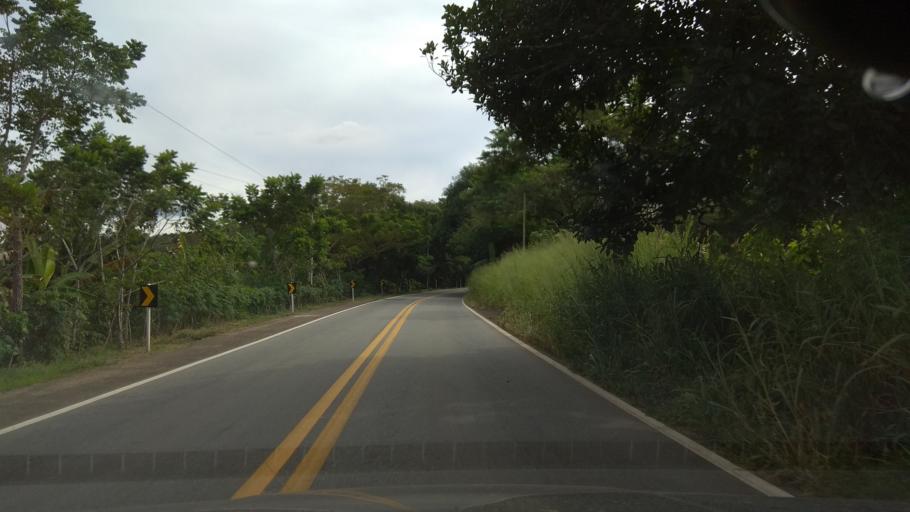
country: BR
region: Bahia
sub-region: Ubata
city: Ubata
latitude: -14.1943
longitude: -39.5543
